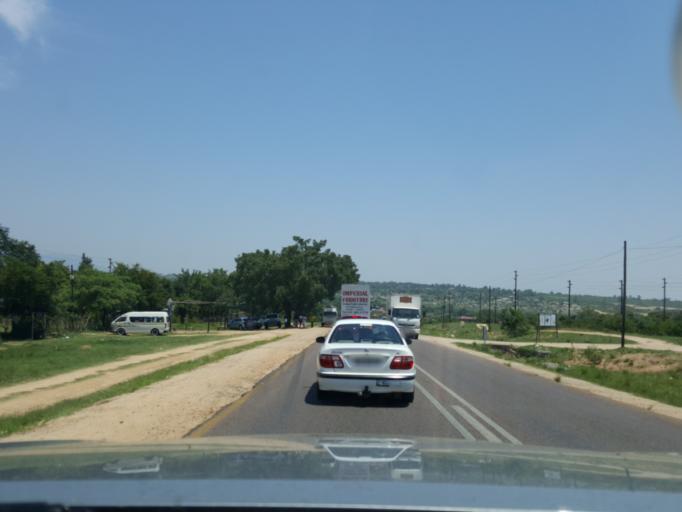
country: ZA
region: Limpopo
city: Thulamahashi
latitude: -24.7941
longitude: 31.0824
